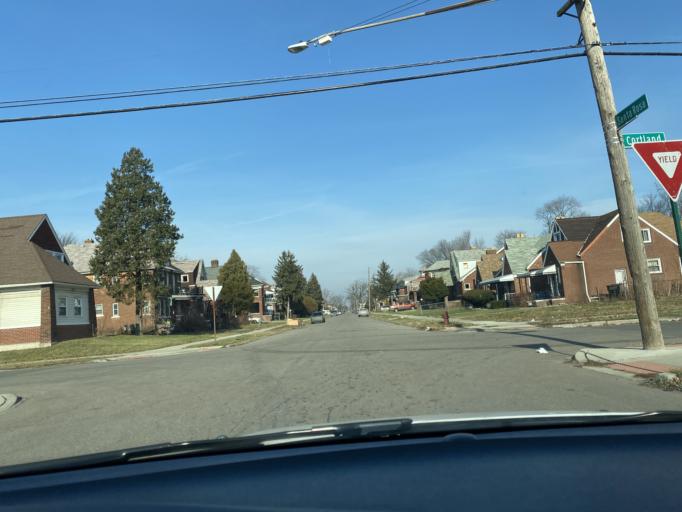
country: US
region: Michigan
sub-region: Wayne County
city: Highland Park
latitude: 42.3791
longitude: -83.1413
